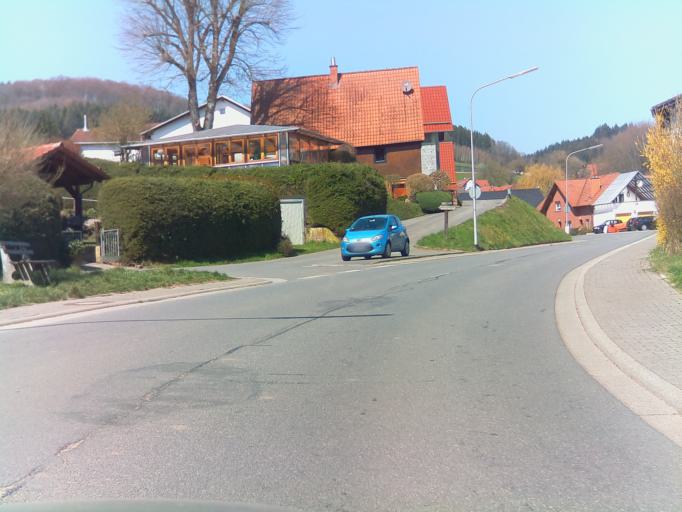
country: DE
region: Hesse
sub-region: Regierungsbezirk Darmstadt
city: Wald-Michelbach
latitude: 49.5835
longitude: 8.8155
